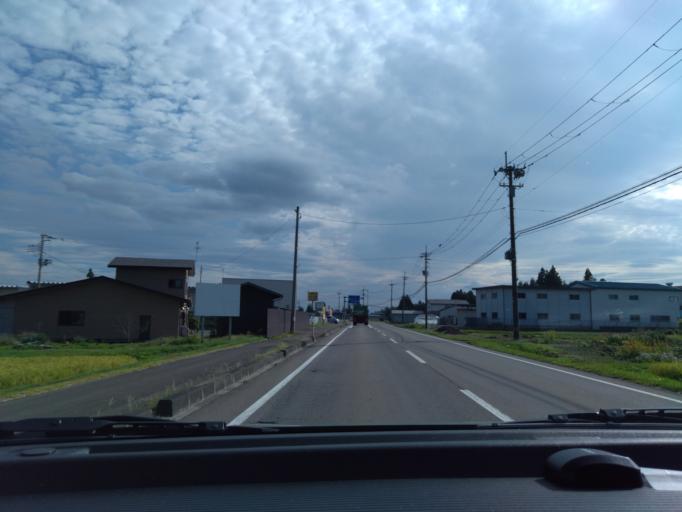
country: JP
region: Iwate
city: Hanamaki
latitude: 39.4534
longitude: 141.0984
